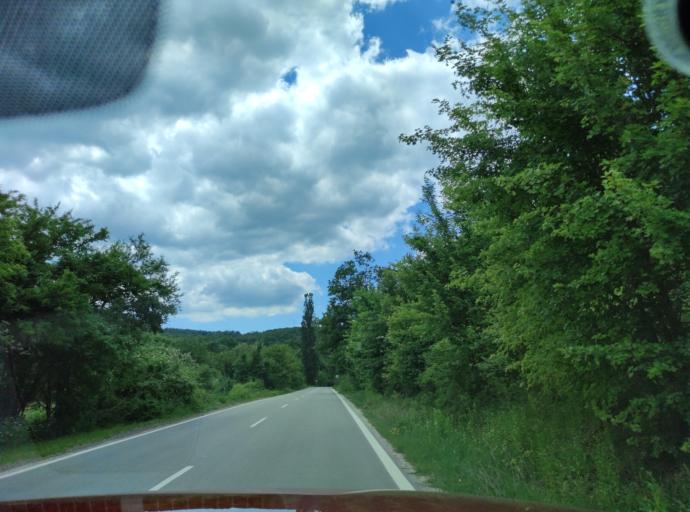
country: BG
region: Montana
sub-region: Obshtina Chiprovtsi
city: Chiprovtsi
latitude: 43.4565
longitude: 22.8992
